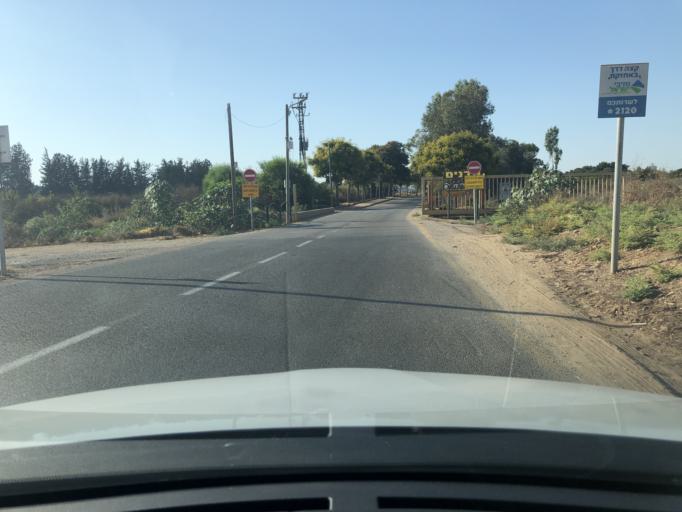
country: IL
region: Central District
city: Hod HaSharon
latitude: 32.1345
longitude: 34.9090
